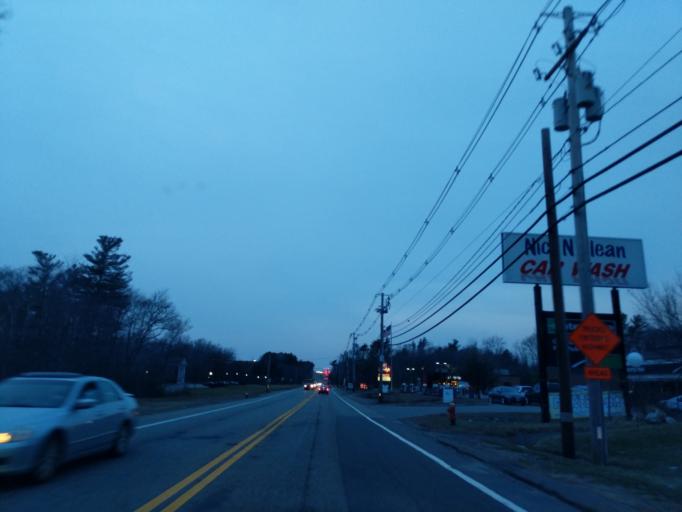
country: US
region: Massachusetts
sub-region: Bristol County
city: Raynham Center
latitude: 41.9051
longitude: -71.0256
